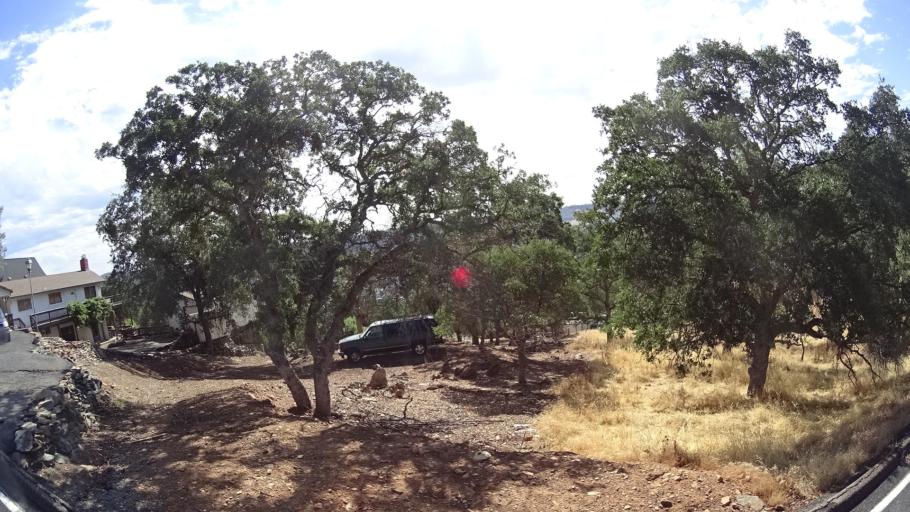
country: US
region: California
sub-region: Calaveras County
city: Copperopolis
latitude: 37.9104
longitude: -120.6085
